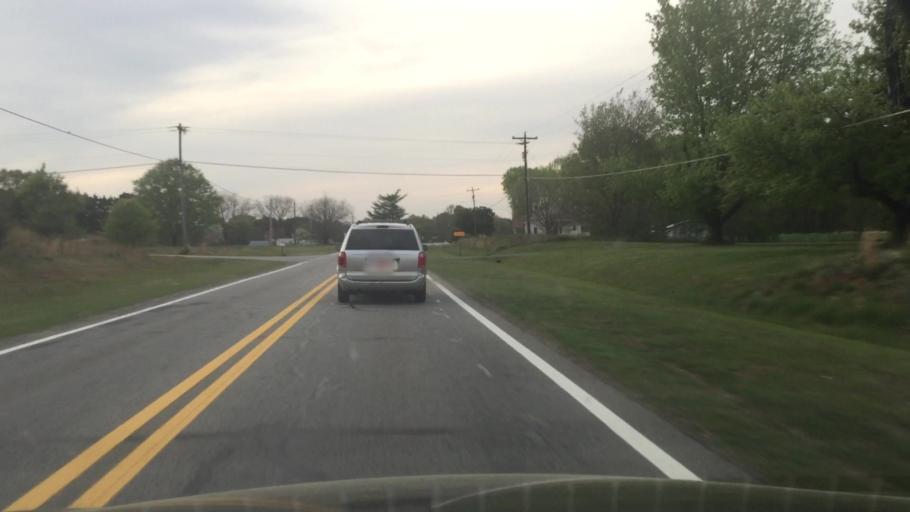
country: US
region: North Carolina
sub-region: Rockingham County
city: Reidsville
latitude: 36.3070
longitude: -79.6253
